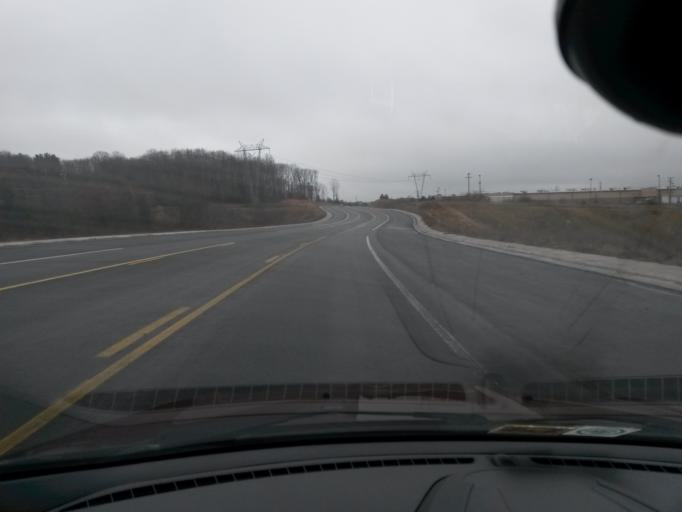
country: US
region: West Virginia
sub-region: Raleigh County
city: Stanaford
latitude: 37.8062
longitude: -81.1748
